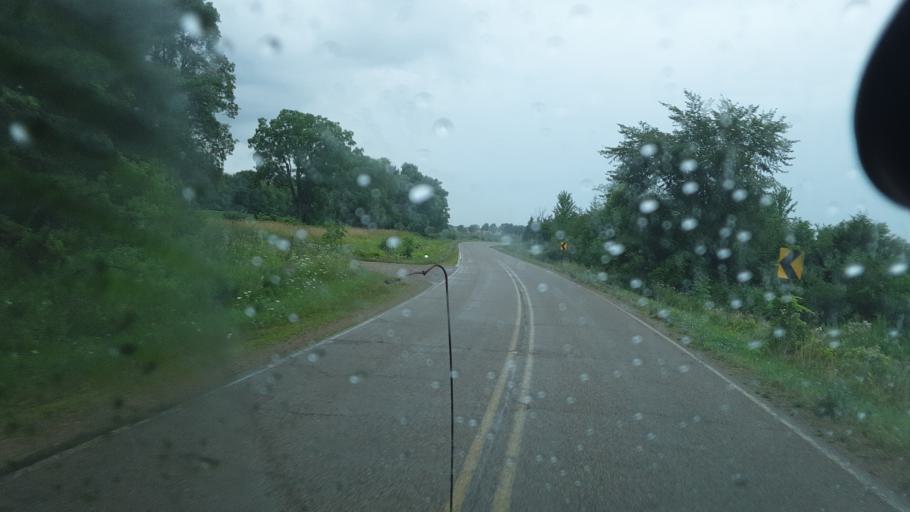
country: US
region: Michigan
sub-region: Hillsdale County
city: Reading
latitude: 41.7085
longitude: -84.7082
